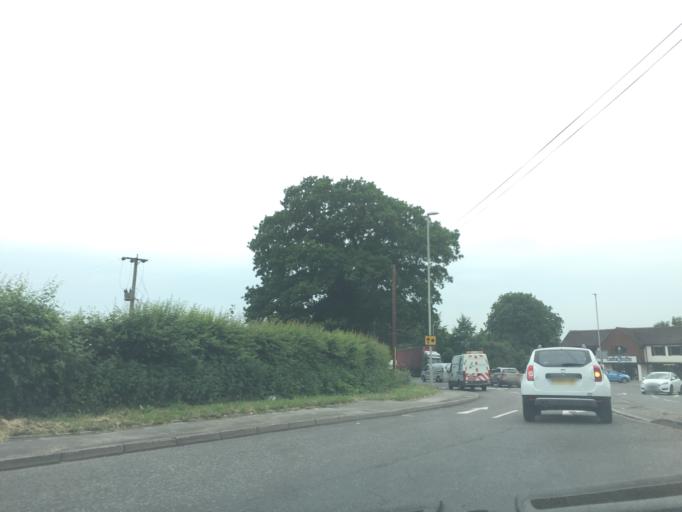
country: GB
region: England
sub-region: Dorset
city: Ferndown
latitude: 50.7866
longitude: -1.9066
